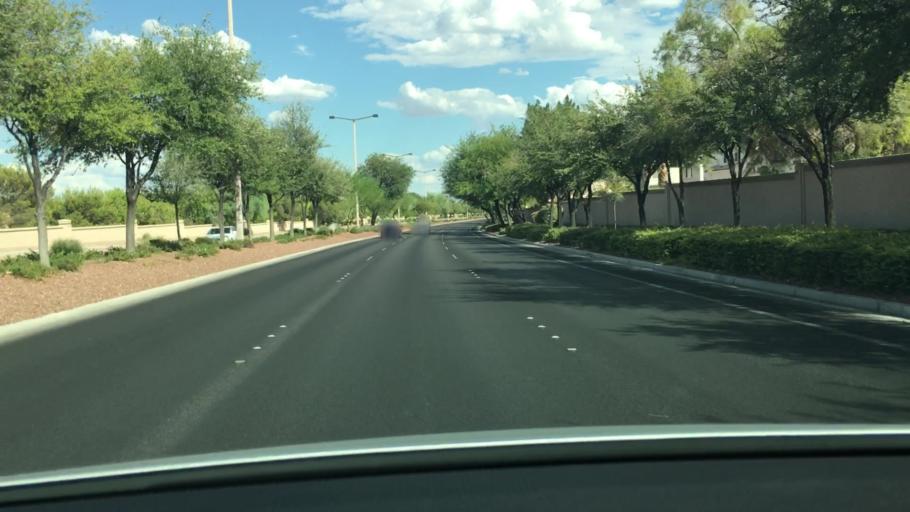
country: US
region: Nevada
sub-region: Clark County
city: Summerlin South
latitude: 36.2052
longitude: -115.2937
